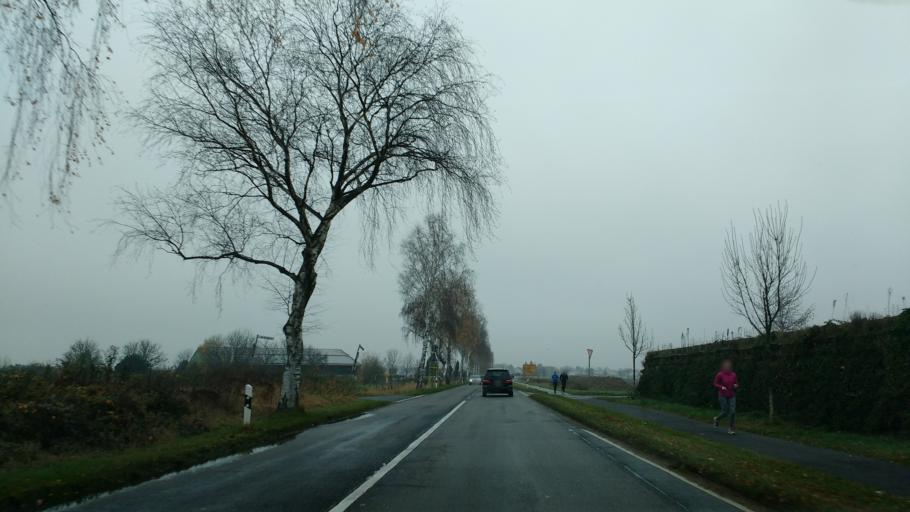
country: DE
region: North Rhine-Westphalia
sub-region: Regierungsbezirk Koln
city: Frechen
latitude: 50.9544
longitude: 6.8289
